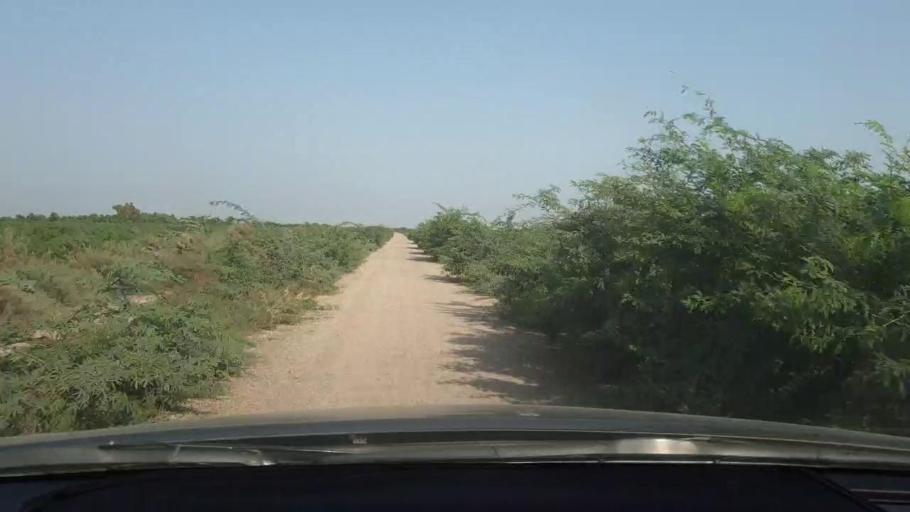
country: PK
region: Sindh
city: Naukot
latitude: 24.7781
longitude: 69.2815
